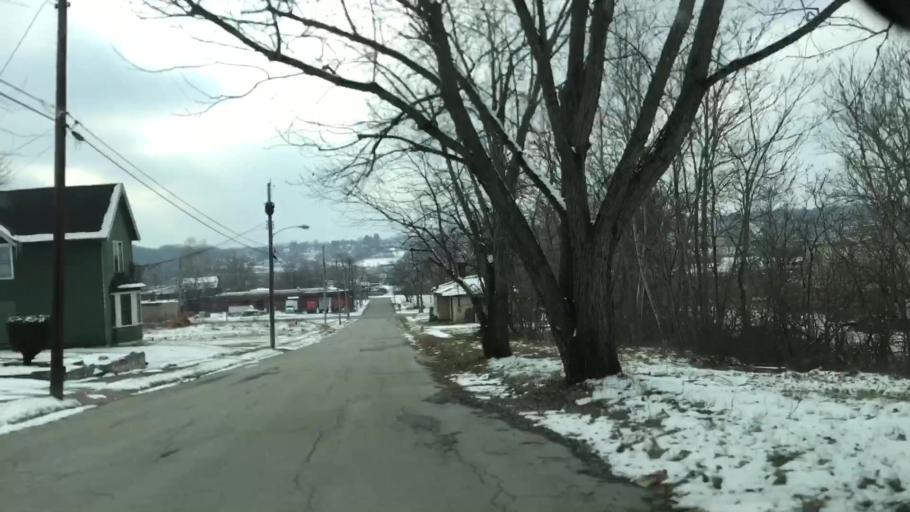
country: US
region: Ohio
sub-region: Mahoning County
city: Campbell
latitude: 41.0859
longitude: -80.6174
